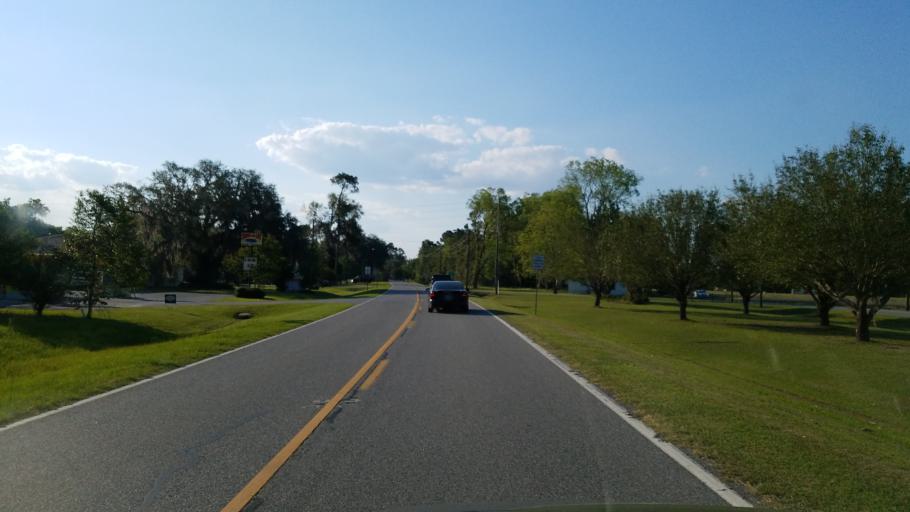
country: US
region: Georgia
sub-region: Lanier County
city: Lakeland
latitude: 31.0256
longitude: -83.0663
